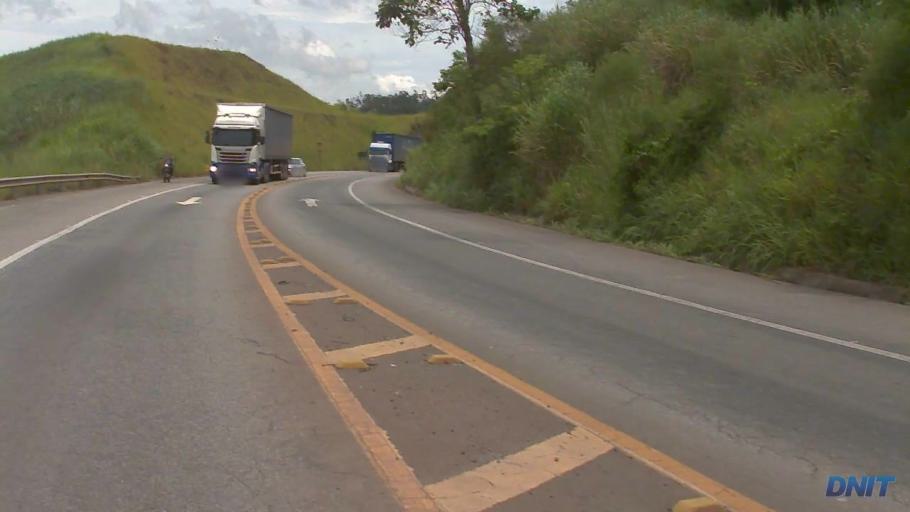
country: BR
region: Minas Gerais
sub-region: Coronel Fabriciano
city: Coronel Fabriciano
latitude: -19.5308
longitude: -42.6033
